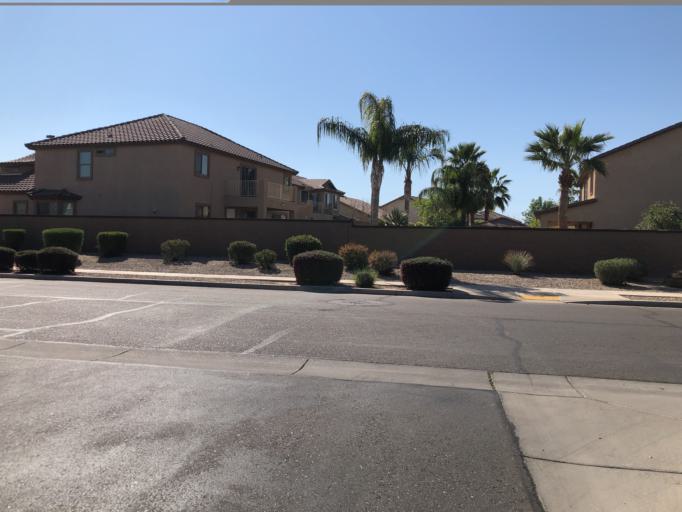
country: US
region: Arizona
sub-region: Maricopa County
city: Queen Creek
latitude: 33.2432
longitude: -111.7150
